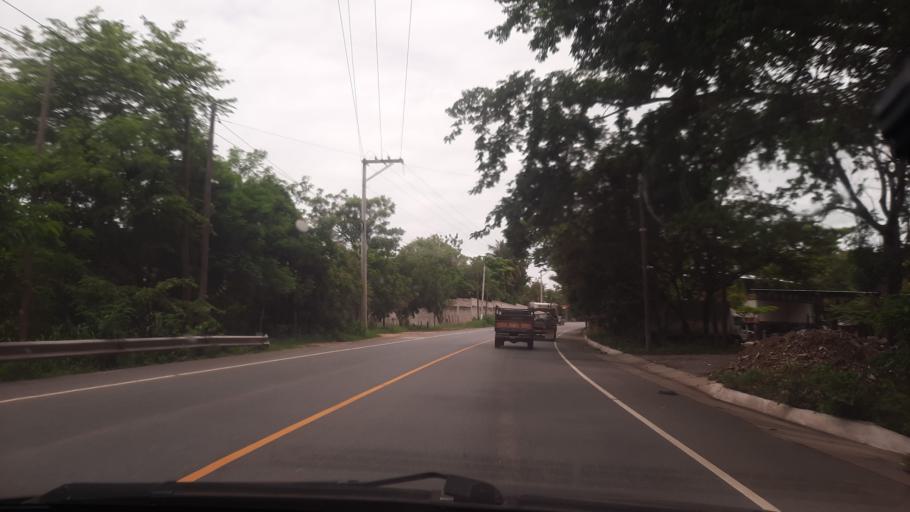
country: GT
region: Zacapa
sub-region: Municipio de Zacapa
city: Gualan
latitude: 15.1323
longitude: -89.3461
